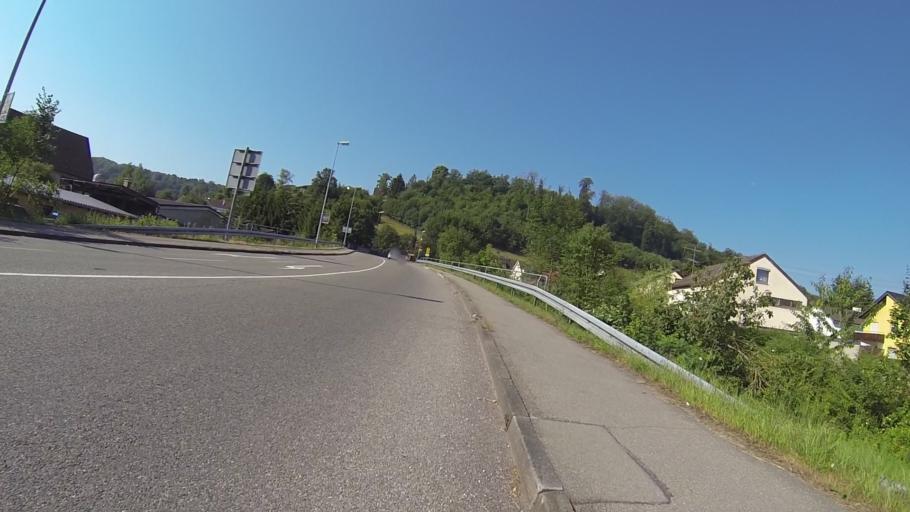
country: DE
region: Baden-Wuerttemberg
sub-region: Regierungsbezirk Stuttgart
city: Konigsbronn
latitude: 48.7428
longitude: 10.1114
